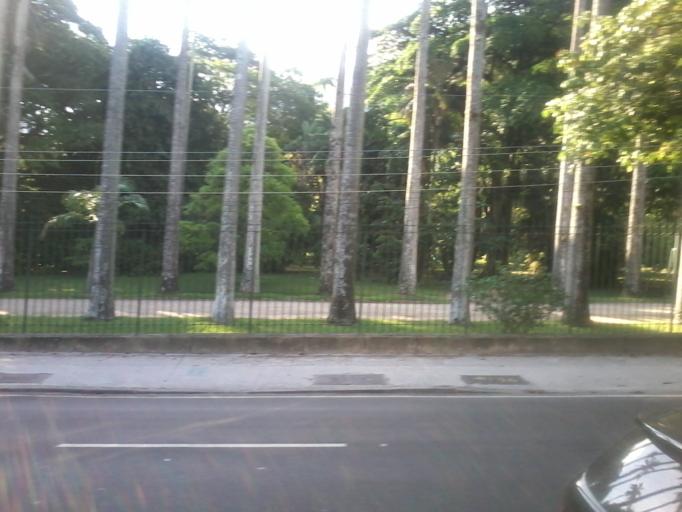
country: BR
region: Rio de Janeiro
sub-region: Rio De Janeiro
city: Rio de Janeiro
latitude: -22.9701
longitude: -43.2224
